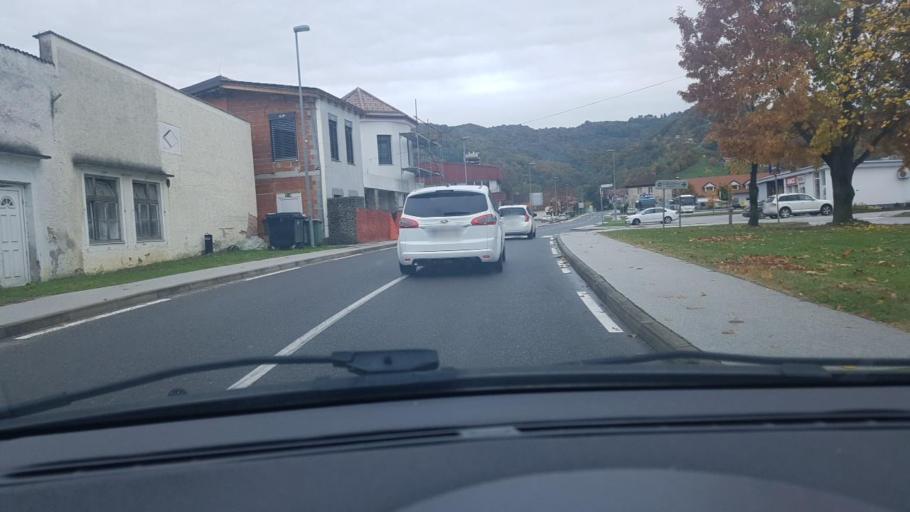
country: SI
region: Majsperk
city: Majsperk
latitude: 46.3398
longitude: 15.7367
